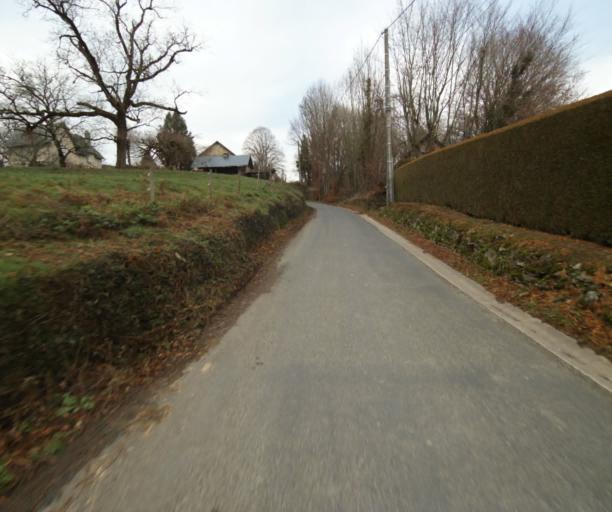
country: FR
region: Limousin
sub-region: Departement de la Correze
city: Chameyrat
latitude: 45.2417
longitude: 1.7231
